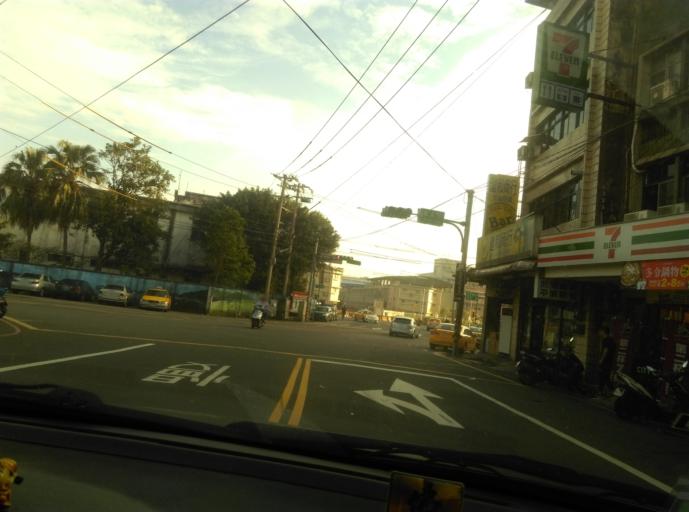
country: TW
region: Taiwan
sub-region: Keelung
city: Keelung
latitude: 25.1455
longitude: 121.7387
